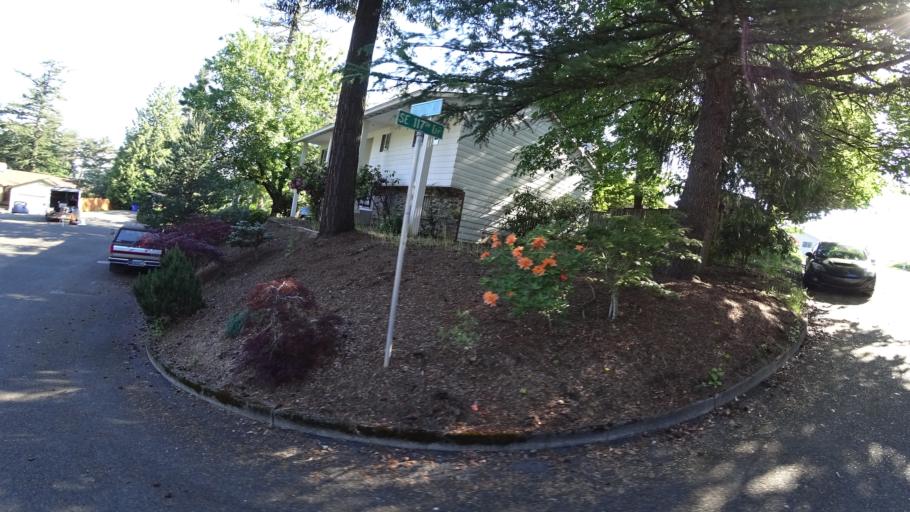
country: US
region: Oregon
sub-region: Clackamas County
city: Happy Valley
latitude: 45.4676
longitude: -122.5435
